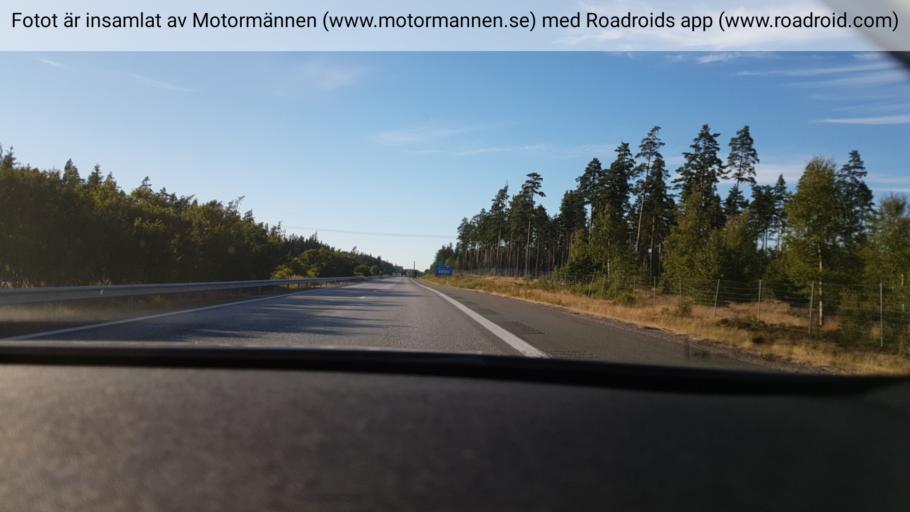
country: SE
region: Joenkoeping
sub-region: Jonkopings Kommun
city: Odensjo
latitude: 57.6522
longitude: 14.1864
